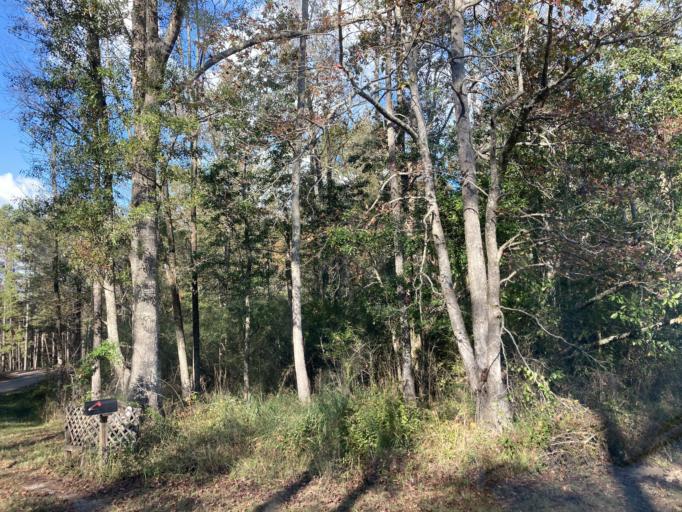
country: US
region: Mississippi
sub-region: Lamar County
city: Sumrall
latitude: 31.4278
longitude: -89.6505
